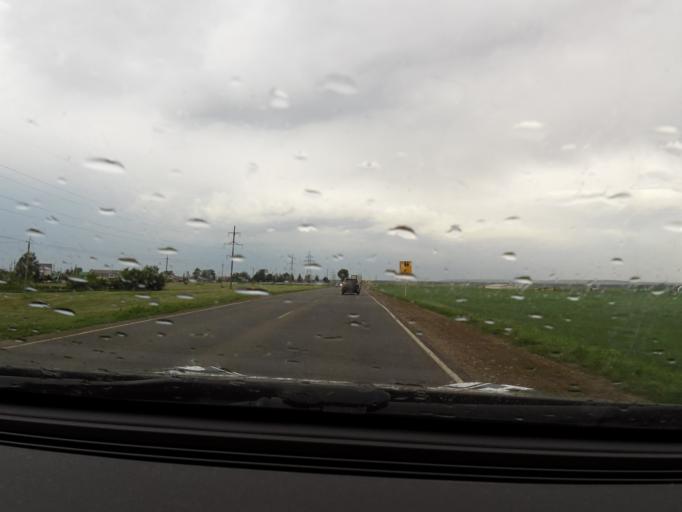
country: RU
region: Bashkortostan
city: Mikhaylovka
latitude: 54.8669
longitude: 55.7451
